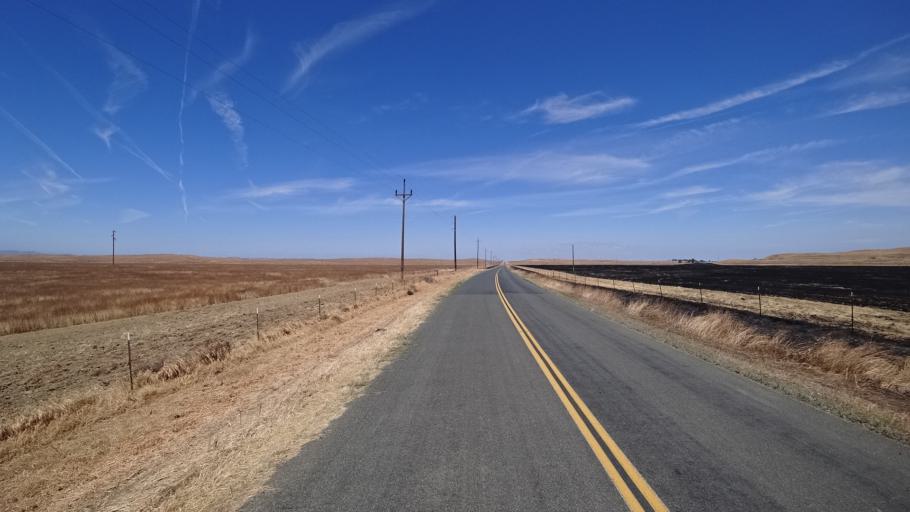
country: US
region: California
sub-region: Kings County
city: Kettleman City
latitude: 35.8346
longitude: -119.9153
